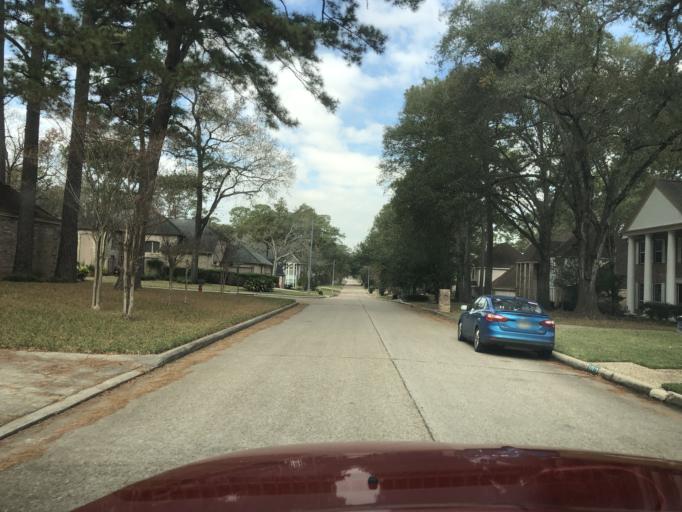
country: US
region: Texas
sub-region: Harris County
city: Spring
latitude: 30.0199
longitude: -95.4635
